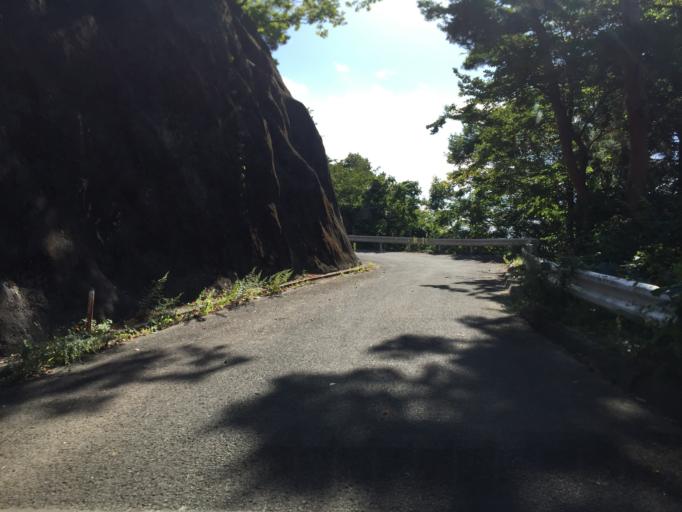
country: JP
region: Fukushima
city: Yanagawamachi-saiwaicho
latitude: 37.8498
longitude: 140.6809
